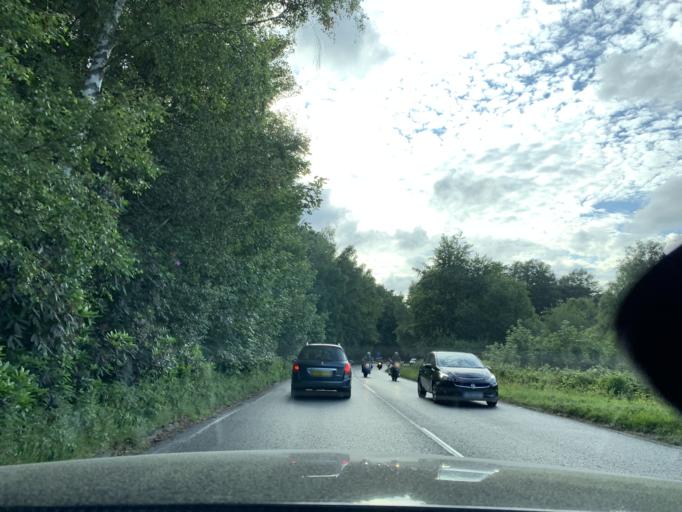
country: GB
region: England
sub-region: East Sussex
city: Robertsbridge
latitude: 50.9586
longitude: 0.4927
